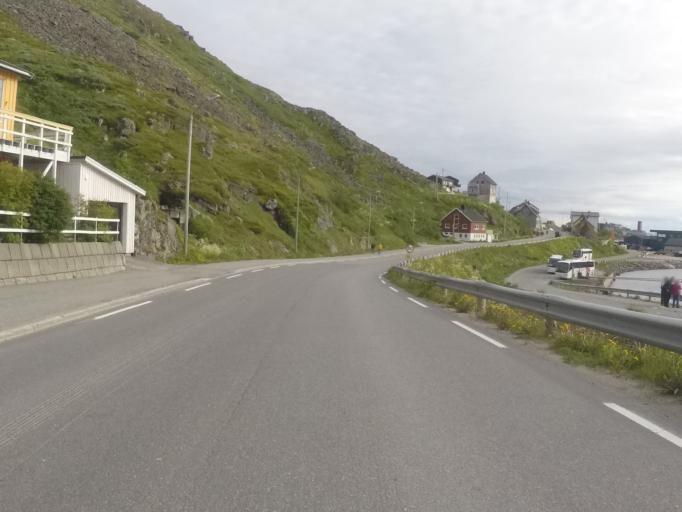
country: NO
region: Finnmark Fylke
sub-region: Nordkapp
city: Honningsvag
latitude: 70.9866
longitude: 25.9669
